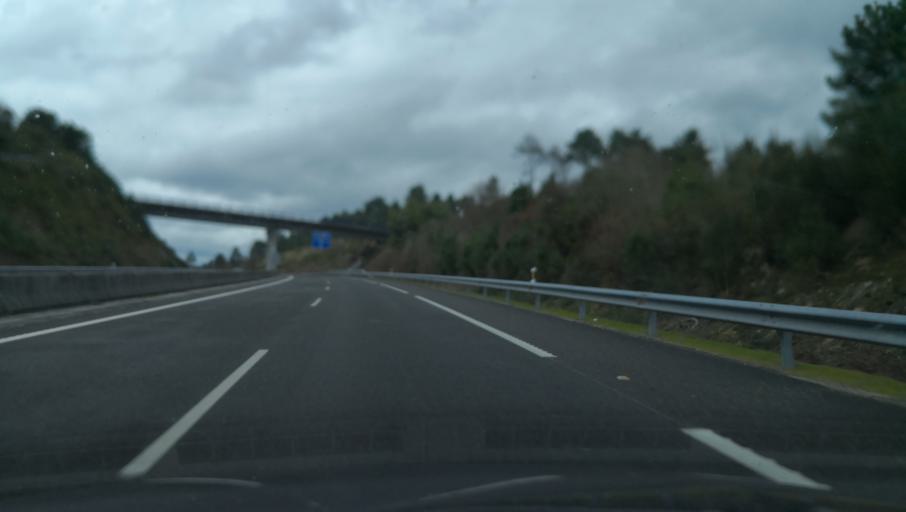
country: ES
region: Galicia
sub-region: Provincia de Ourense
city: Maside
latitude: 42.4404
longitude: -8.0179
